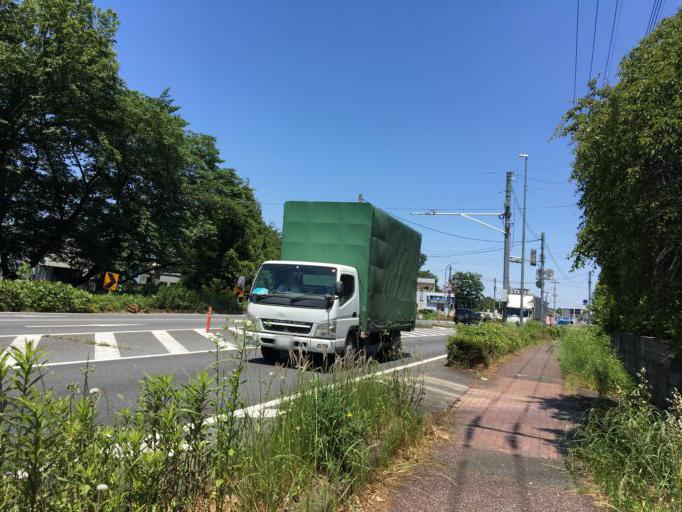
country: JP
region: Saitama
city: Sakado
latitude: 35.9312
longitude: 139.3854
